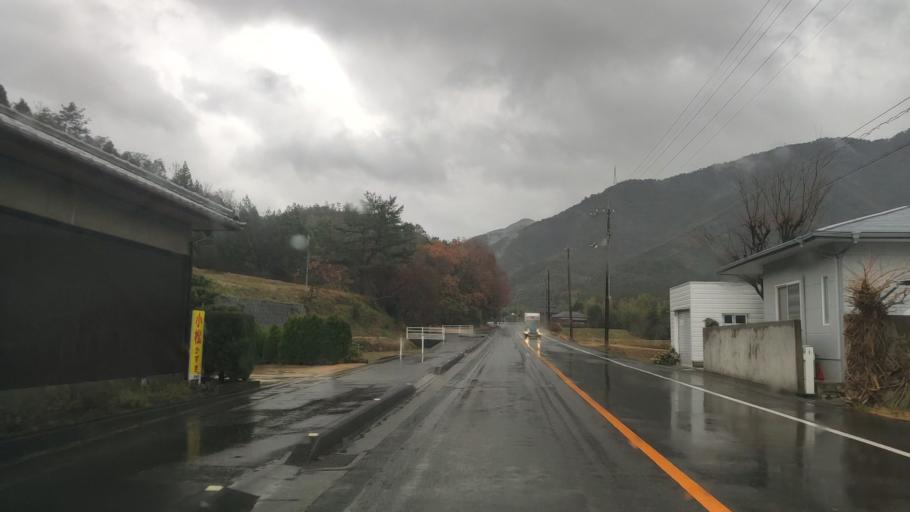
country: JP
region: Tokushima
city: Kamojimacho-jogejima
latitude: 34.2012
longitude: 134.3302
